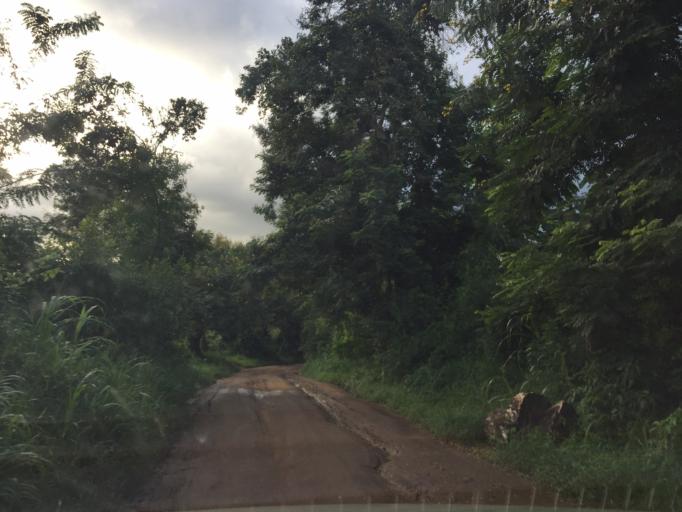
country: TZ
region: Tanga
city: Muheza
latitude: -5.1630
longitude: 38.7712
